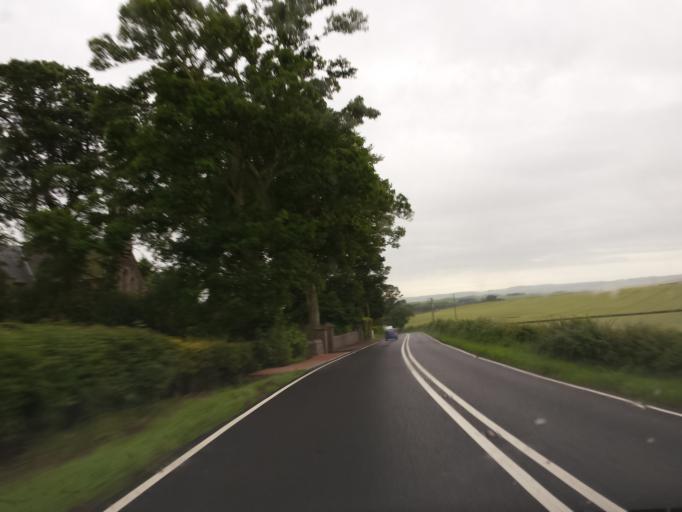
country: GB
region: Scotland
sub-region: Fife
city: Newport-On-Tay
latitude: 56.4241
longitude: -2.9227
